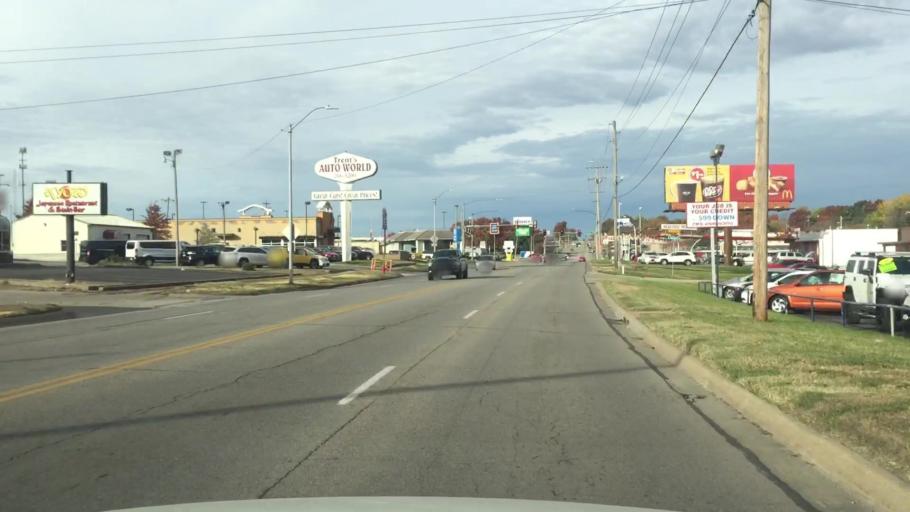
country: US
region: Kansas
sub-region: Shawnee County
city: Topeka
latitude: 39.0153
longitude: -95.6799
